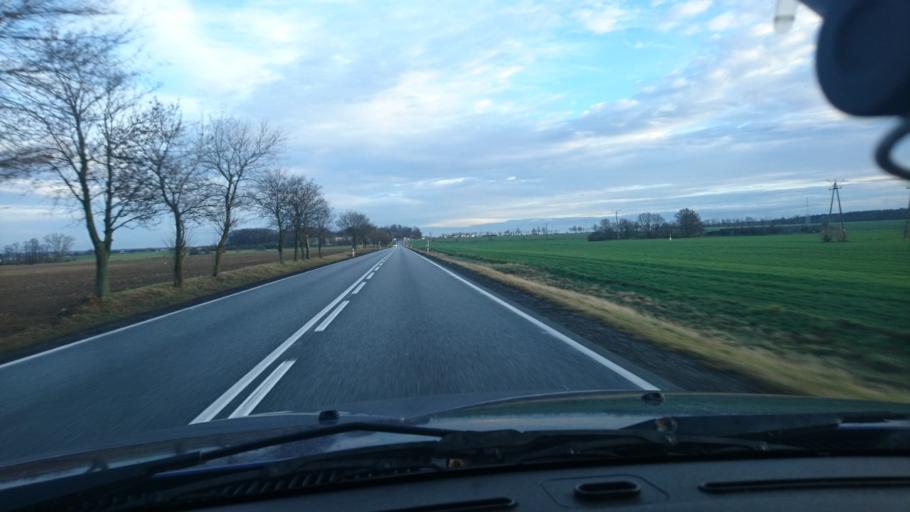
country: PL
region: Greater Poland Voivodeship
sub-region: Powiat kepinski
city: Slupia pod Kepnem
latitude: 51.2451
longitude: 18.0213
